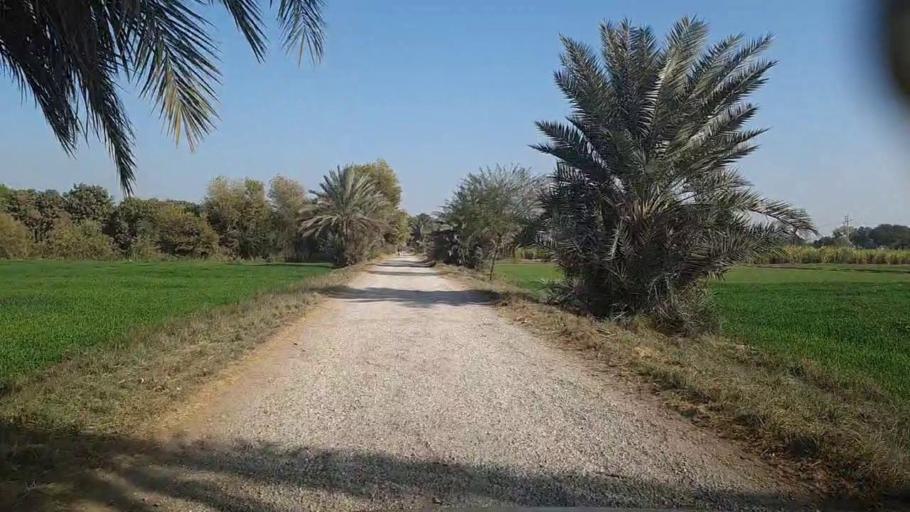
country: PK
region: Sindh
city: Khairpur
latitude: 28.0595
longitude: 69.6897
